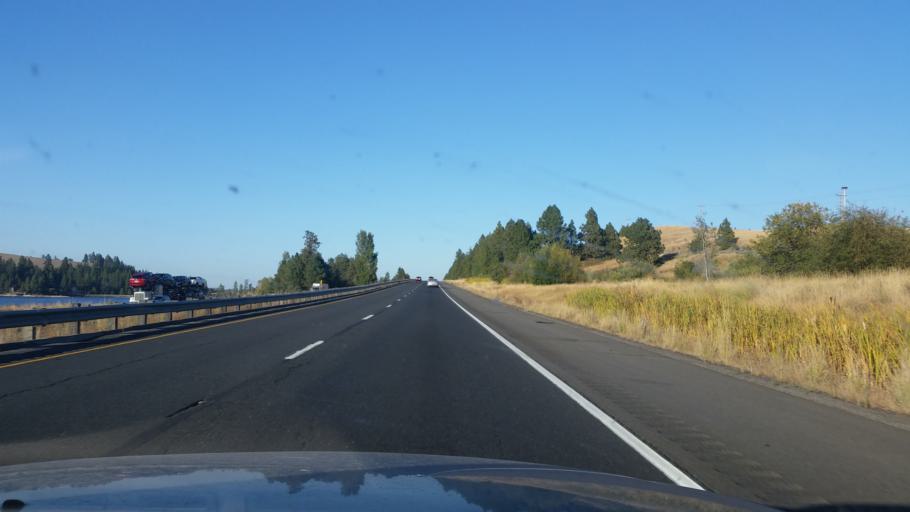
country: US
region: Washington
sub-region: Spokane County
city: Medical Lake
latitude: 47.5451
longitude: -117.6306
